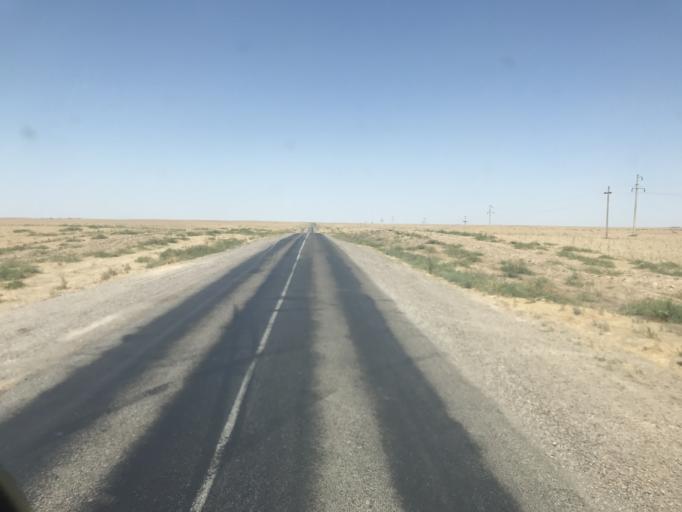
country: UZ
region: Toshkent
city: Chinoz
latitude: 41.1428
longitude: 68.6986
